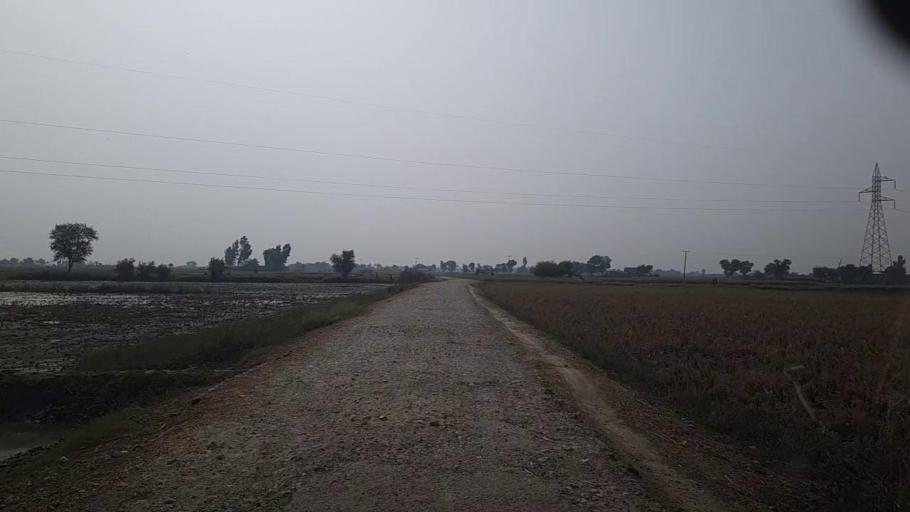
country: PK
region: Sindh
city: Kashmor
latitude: 28.3936
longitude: 69.4220
